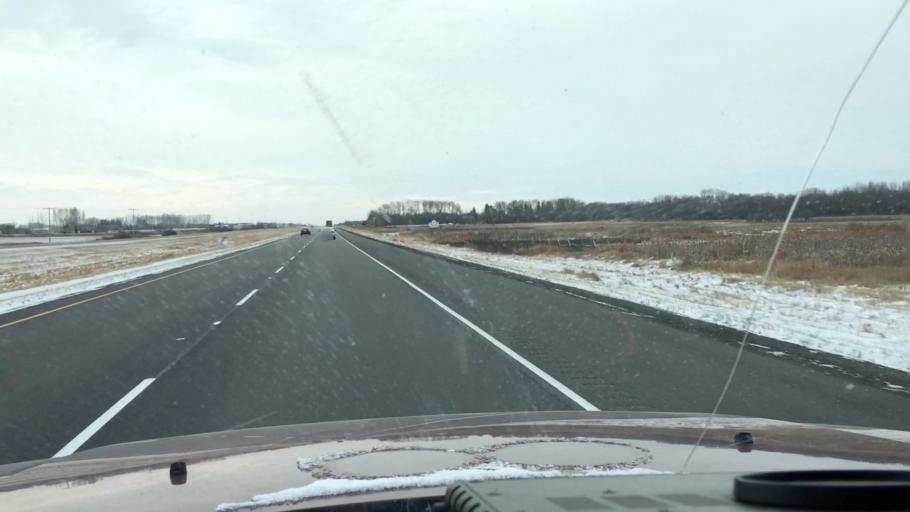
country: CA
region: Saskatchewan
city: Saskatoon
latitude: 51.9800
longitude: -106.5587
